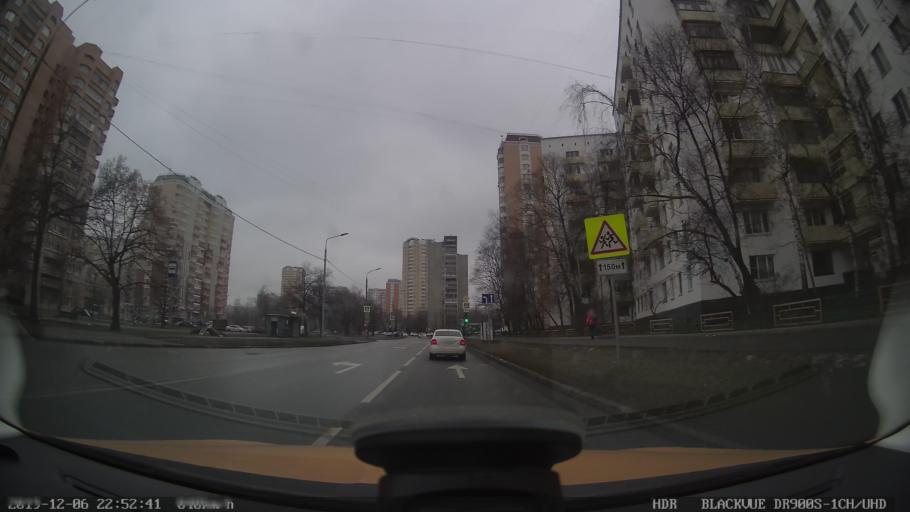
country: RU
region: Moskovskaya
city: Vostochnoe Degunino
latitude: 55.8711
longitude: 37.5548
